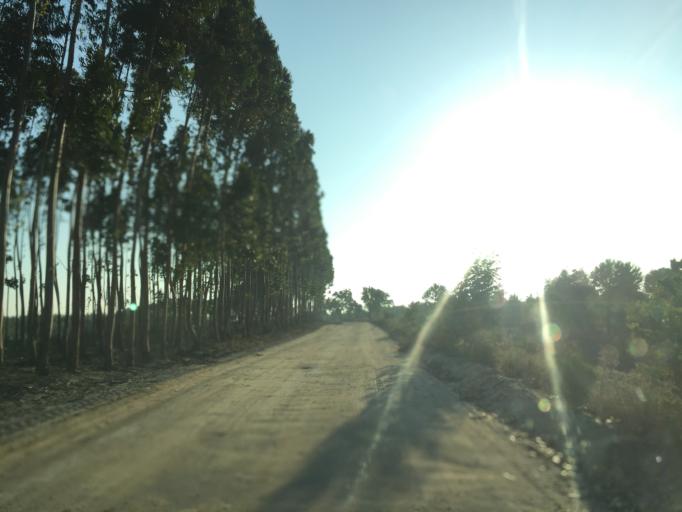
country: PT
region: Portalegre
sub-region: Ponte de Sor
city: Santo Andre
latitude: 39.1236
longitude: -8.3256
